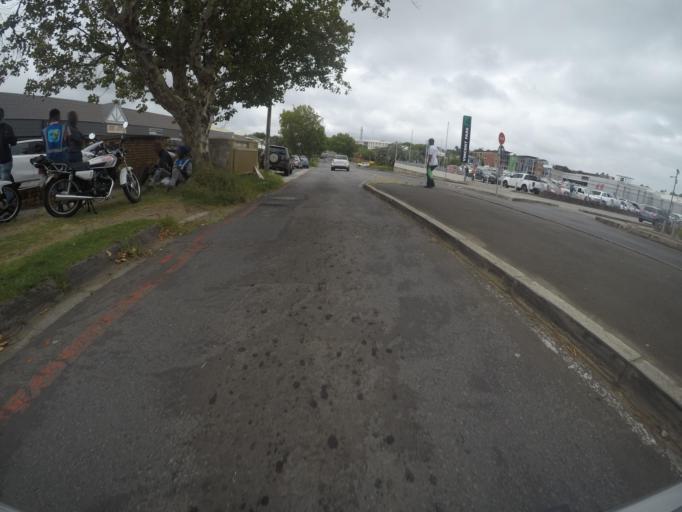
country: ZA
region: Eastern Cape
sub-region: Buffalo City Metropolitan Municipality
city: East London
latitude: -32.9835
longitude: 27.9021
